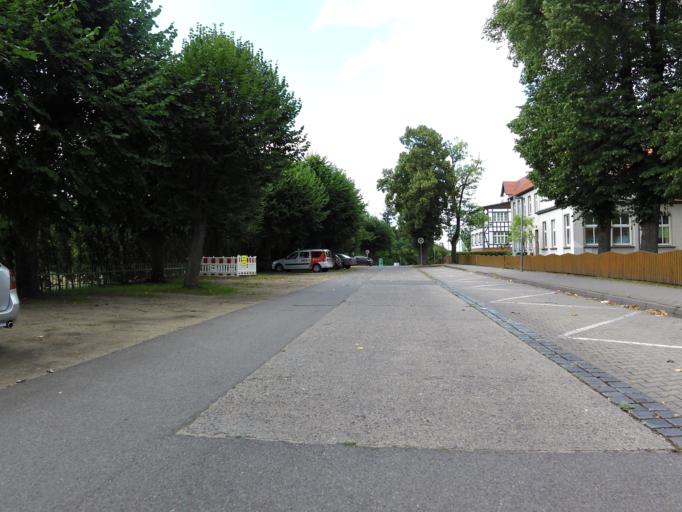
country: DE
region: Brandenburg
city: Lychen
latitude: 53.2039
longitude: 13.3218
